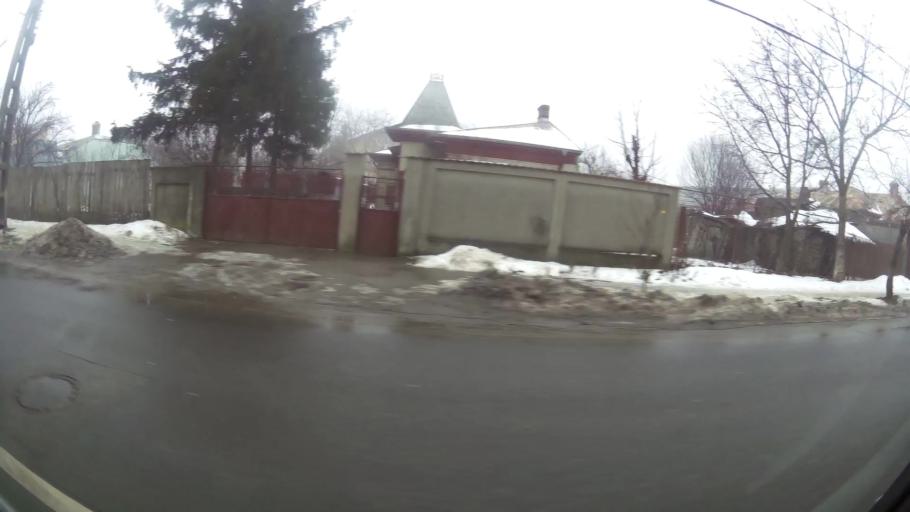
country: RO
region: Ilfov
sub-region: Comuna Chiajna
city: Chiajna
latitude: 44.4600
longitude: 25.9861
